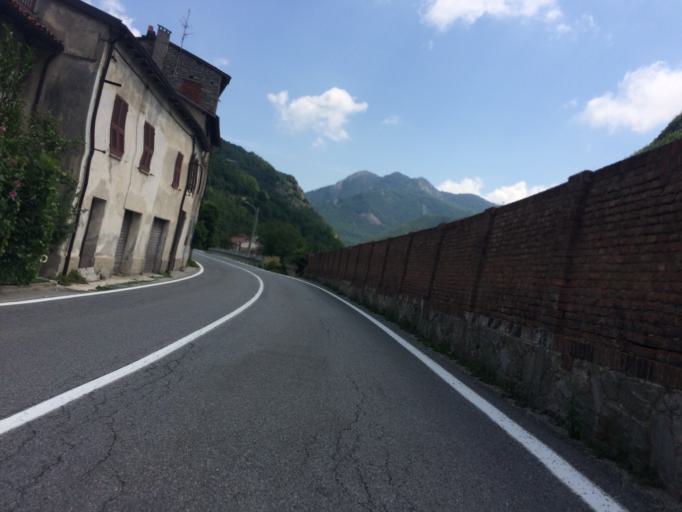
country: IT
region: Piedmont
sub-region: Provincia di Cuneo
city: Ormea
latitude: 44.1583
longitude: 7.9559
